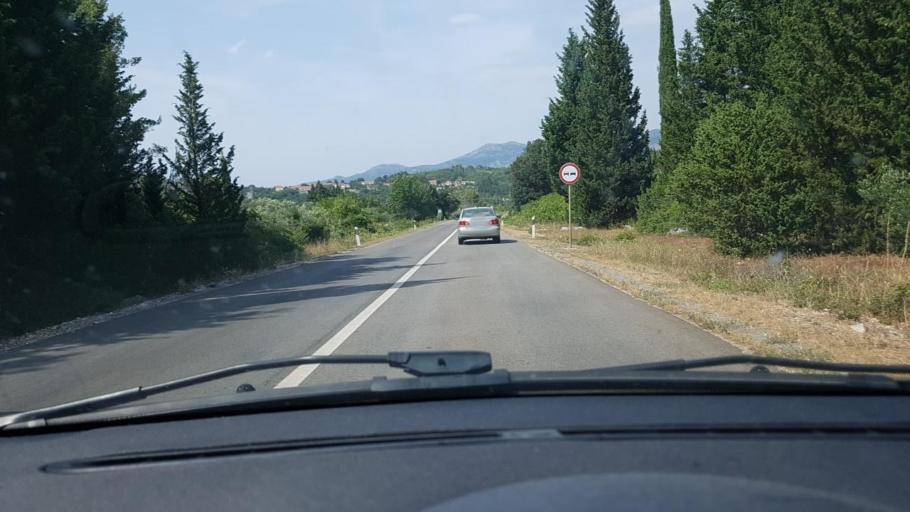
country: HR
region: Dubrovacko-Neretvanska
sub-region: Grad Korcula
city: Zrnovo
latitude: 42.9414
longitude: 17.1048
